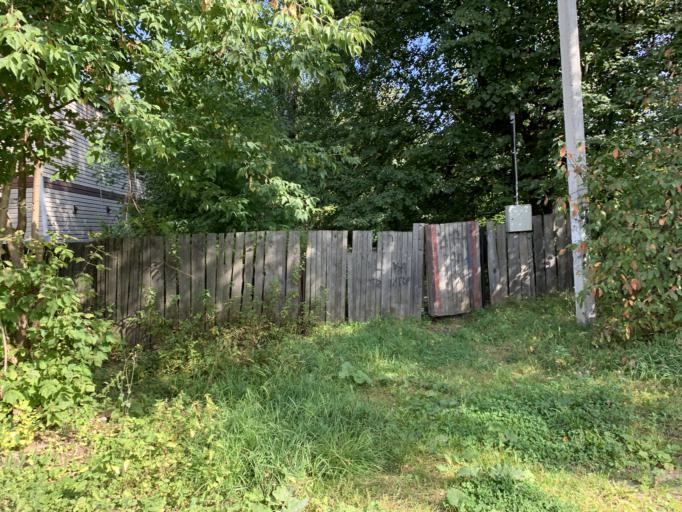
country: RU
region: Moskovskaya
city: Lesnyye Polyany
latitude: 55.9841
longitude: 37.8504
